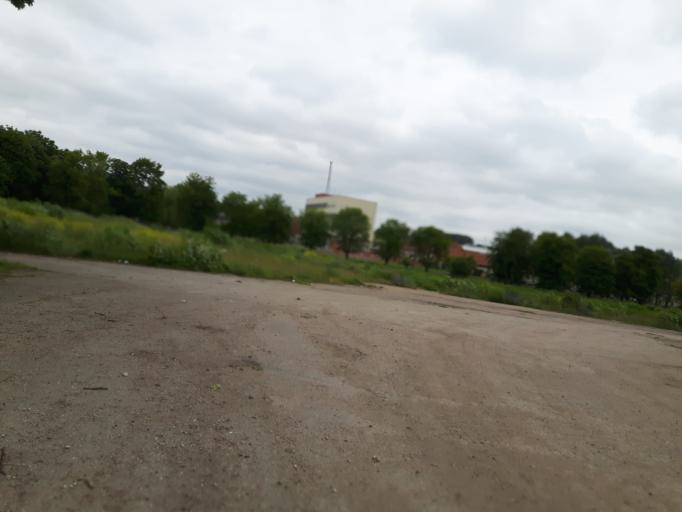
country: LT
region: Klaipedos apskritis
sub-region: Klaipeda
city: Klaipeda
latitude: 55.7101
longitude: 21.1413
